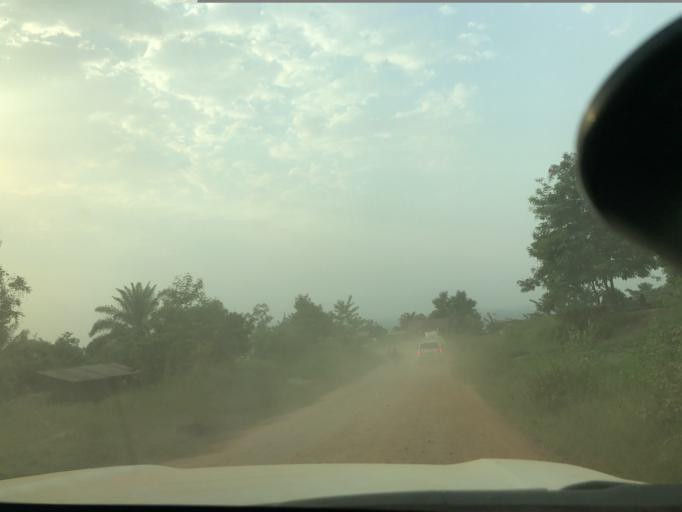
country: CD
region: Nord Kivu
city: Beni
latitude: 0.3493
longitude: 29.6527
